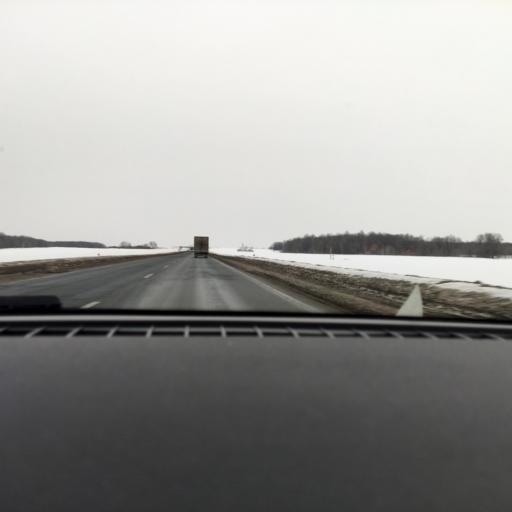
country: RU
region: Samara
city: Petra-Dubrava
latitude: 53.3251
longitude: 50.4548
